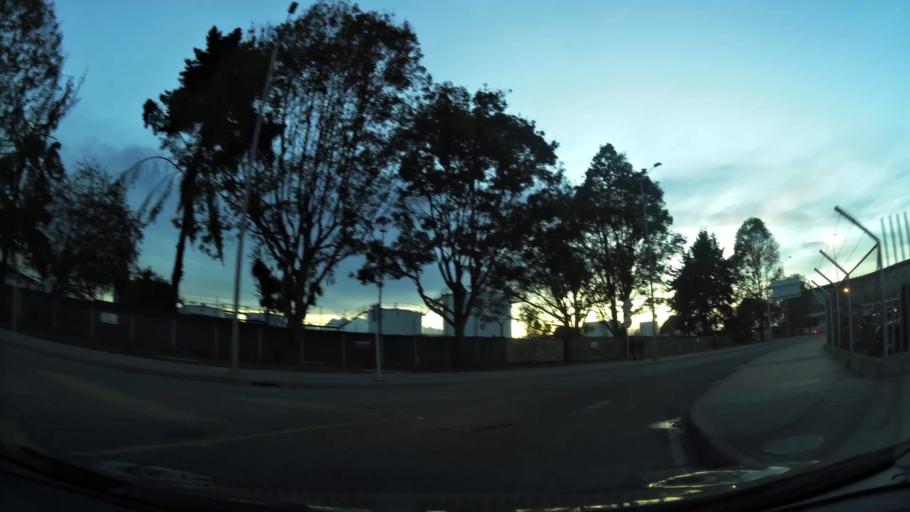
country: CO
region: Cundinamarca
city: Funza
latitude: 4.6958
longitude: -74.1412
